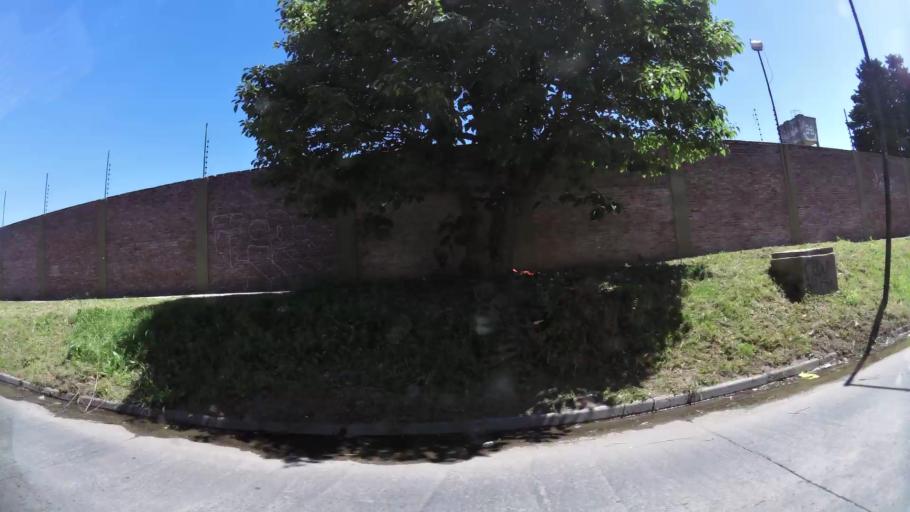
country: AR
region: Buenos Aires
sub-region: Partido de General San Martin
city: General San Martin
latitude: -34.5143
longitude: -58.5611
